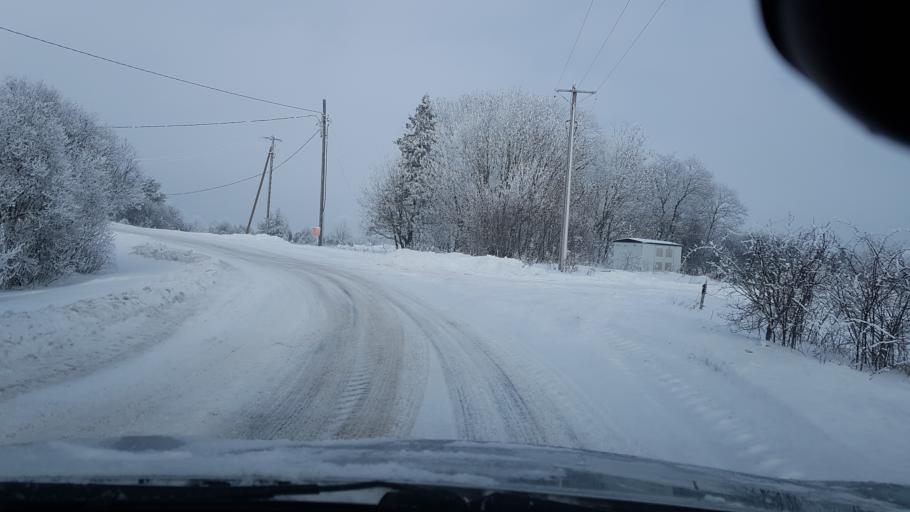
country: EE
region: Harju
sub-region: Keila linn
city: Keila
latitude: 59.3361
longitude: 24.4507
